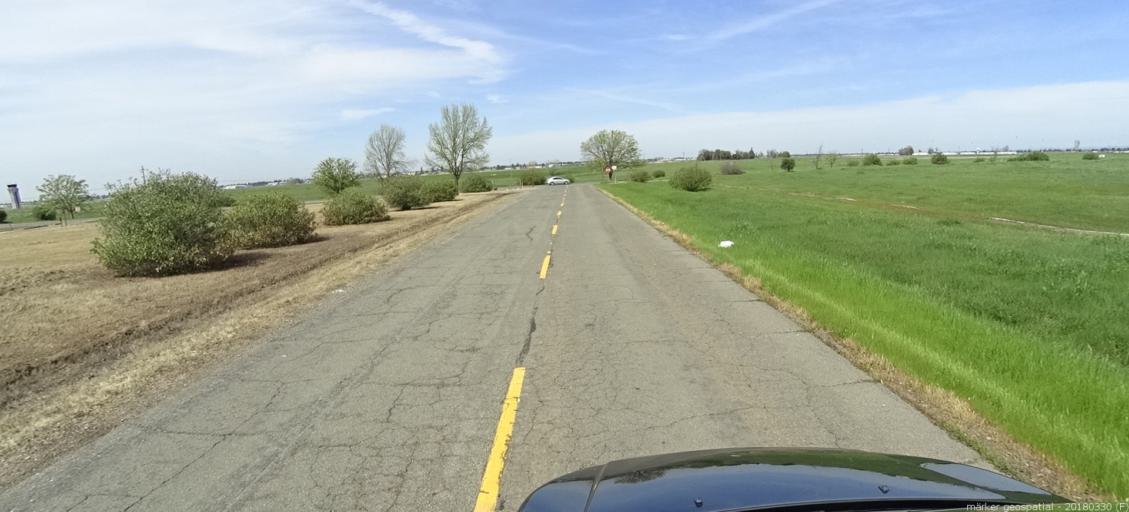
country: US
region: California
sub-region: Sacramento County
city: Rancho Cordova
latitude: 38.5510
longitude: -121.2783
